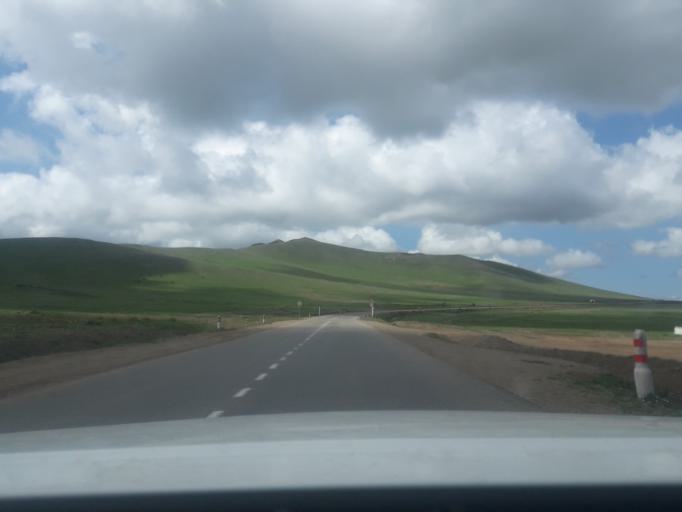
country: MN
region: Central Aimak
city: Altanbulag
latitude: 47.8996
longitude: 106.4234
